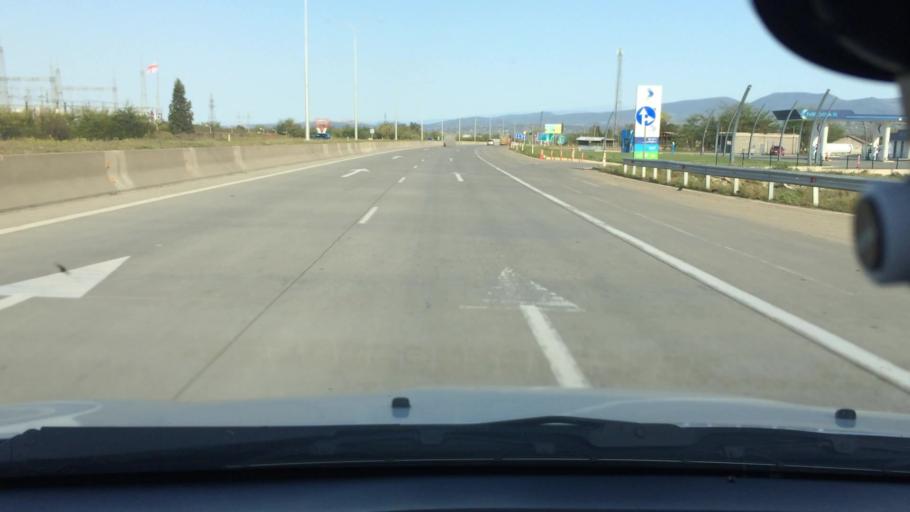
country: GE
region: Imereti
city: Zestap'oni
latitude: 42.1480
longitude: 42.9638
